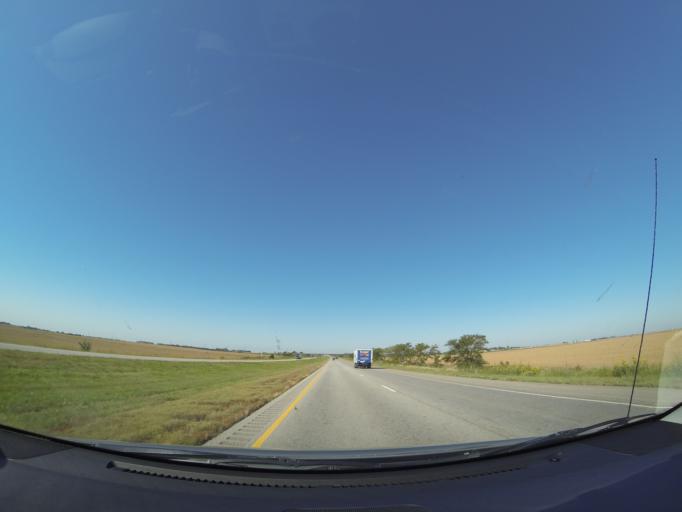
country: US
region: Nebraska
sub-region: Seward County
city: Seward
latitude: 40.8226
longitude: -97.2471
